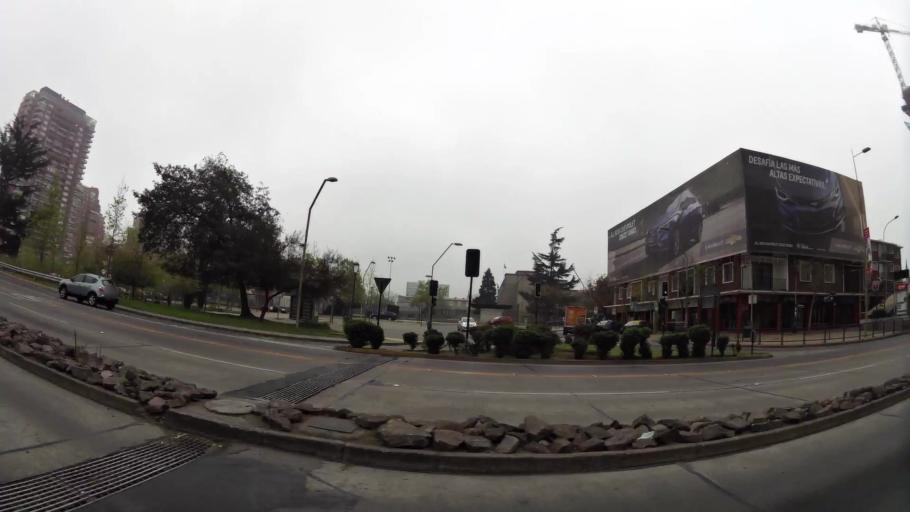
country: CL
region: Santiago Metropolitan
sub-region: Provincia de Santiago
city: Villa Presidente Frei, Nunoa, Santiago, Chile
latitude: -33.4137
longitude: -70.5830
